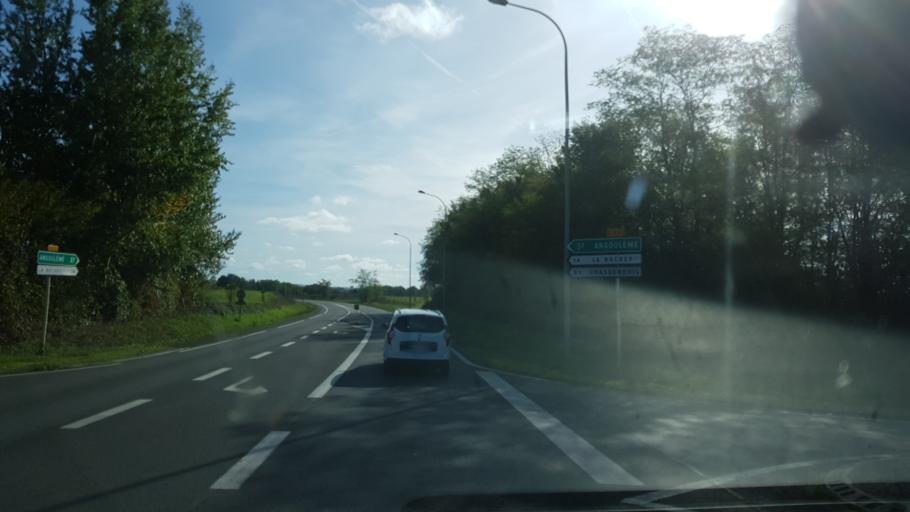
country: FR
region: Poitou-Charentes
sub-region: Departement de la Charente
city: Chasseneuil-sur-Bonnieure
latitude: 45.8438
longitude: 0.4605
